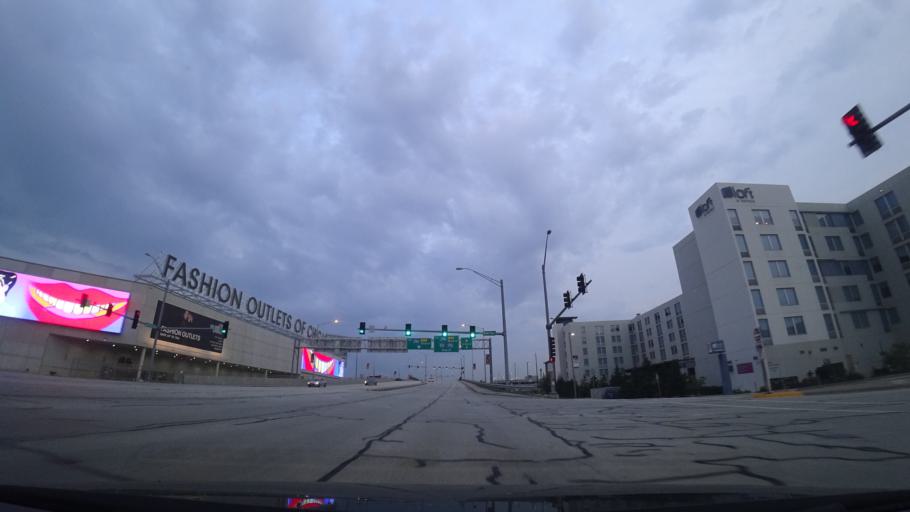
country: US
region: Illinois
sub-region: Cook County
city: Schiller Park
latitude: 41.9769
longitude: -87.8662
